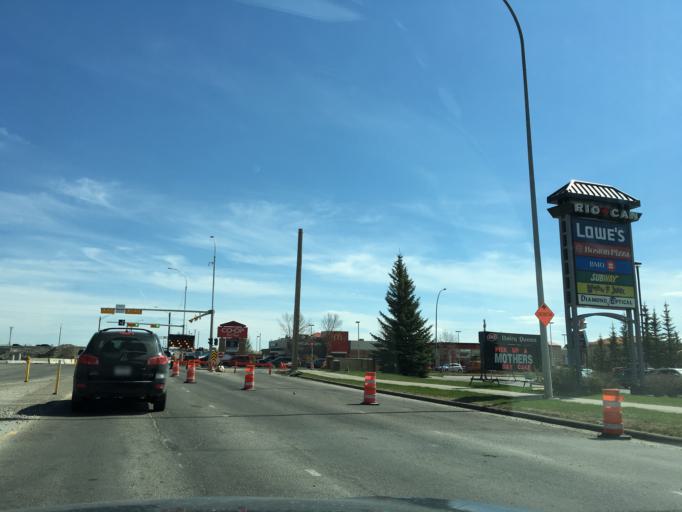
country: CA
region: Alberta
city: Calgary
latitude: 50.9038
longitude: -114.0672
